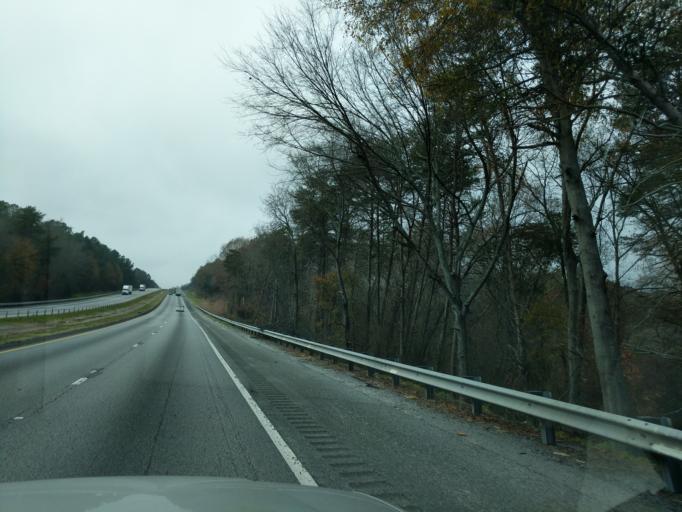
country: US
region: South Carolina
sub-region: Anderson County
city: Centerville
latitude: 34.5640
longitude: -82.7530
